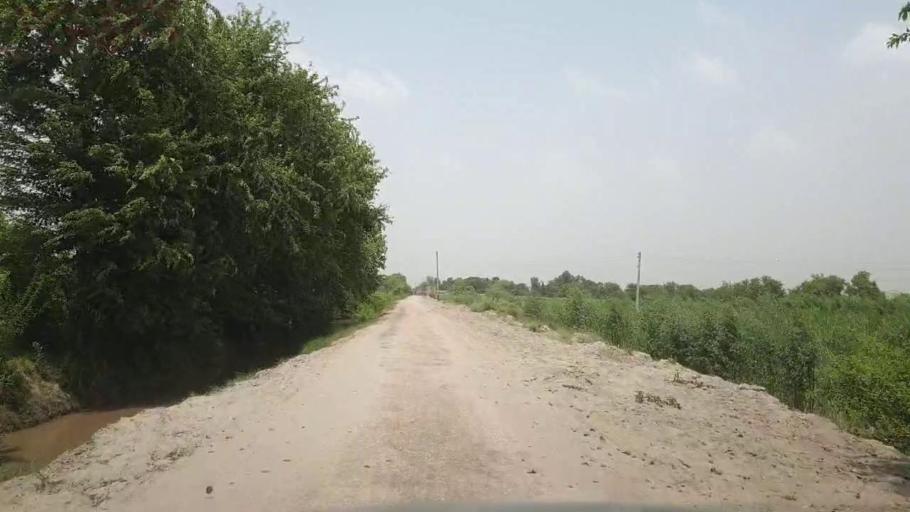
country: PK
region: Sindh
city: Sobhadero
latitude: 27.4342
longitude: 68.4123
